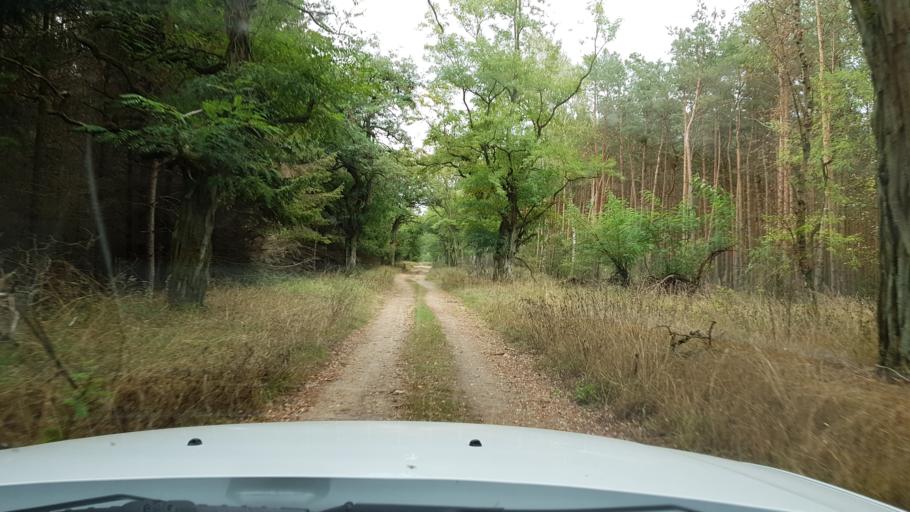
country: PL
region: West Pomeranian Voivodeship
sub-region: Powiat gryfinski
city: Cedynia
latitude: 52.8413
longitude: 14.2641
